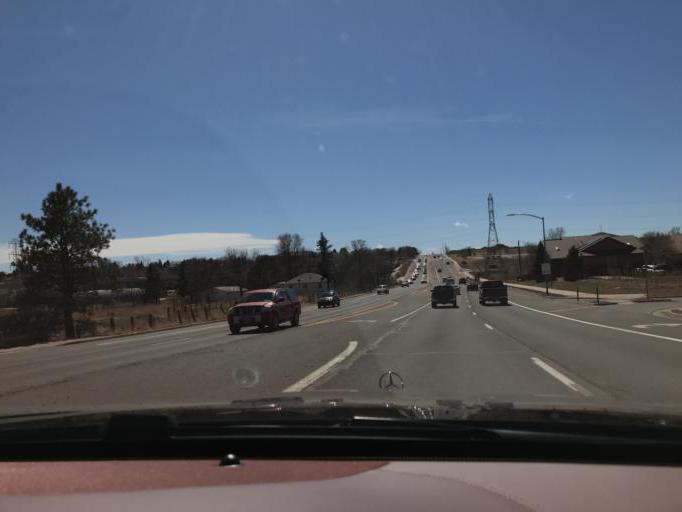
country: US
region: Colorado
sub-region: Jefferson County
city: Applewood
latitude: 39.8005
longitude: -105.1380
